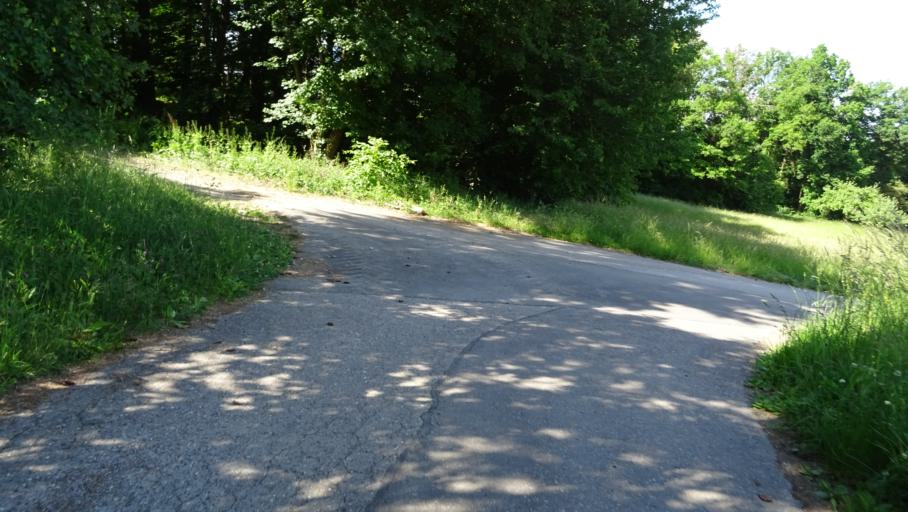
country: DE
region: Baden-Wuerttemberg
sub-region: Karlsruhe Region
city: Seckach
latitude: 49.4319
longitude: 9.3555
